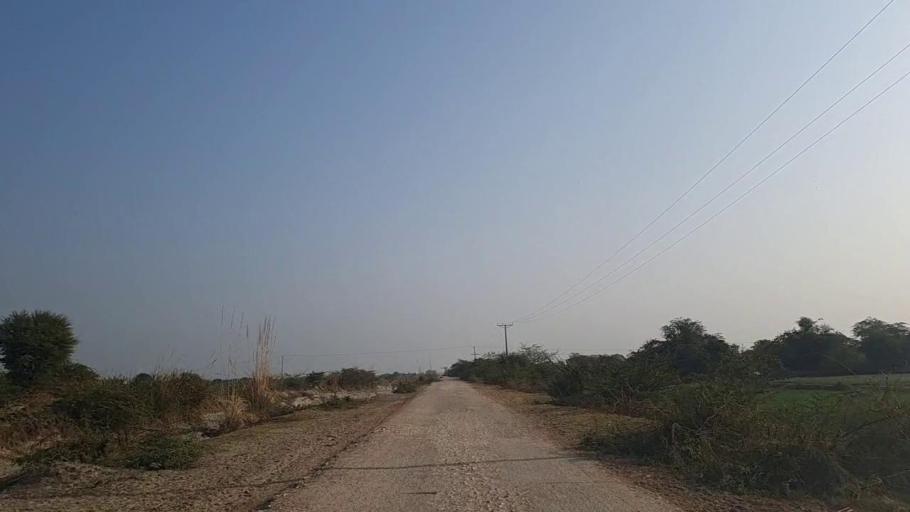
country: PK
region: Sindh
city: Jam Sahib
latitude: 26.2378
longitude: 68.5909
